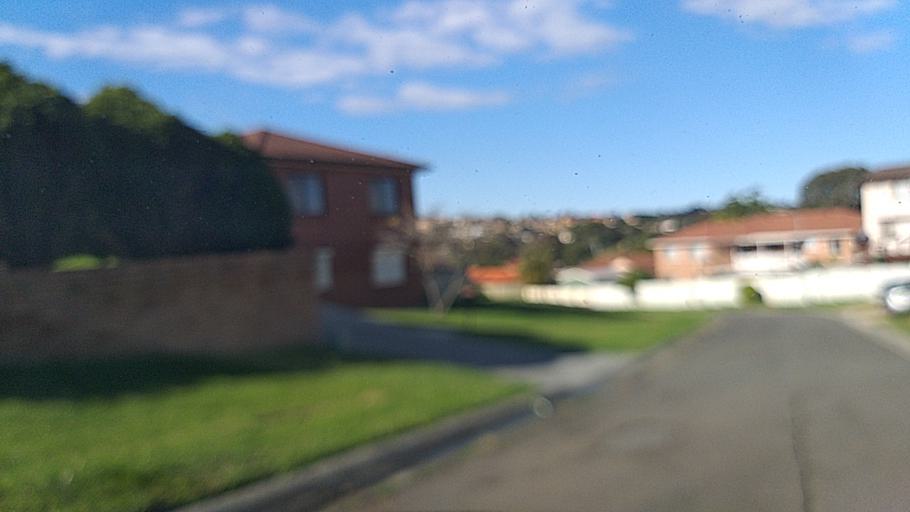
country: AU
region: New South Wales
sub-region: Wollongong
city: Berkeley
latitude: -34.4744
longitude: 150.8492
